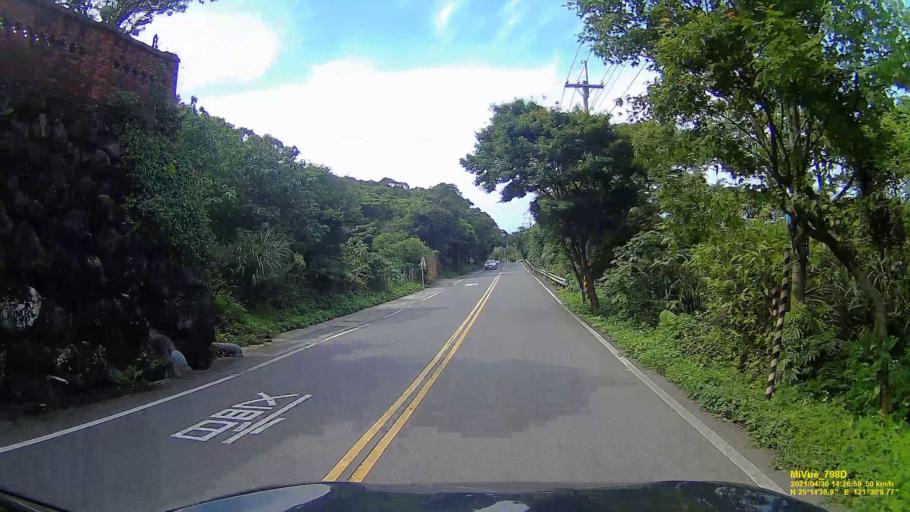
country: TW
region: Taipei
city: Taipei
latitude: 25.2440
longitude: 121.5027
